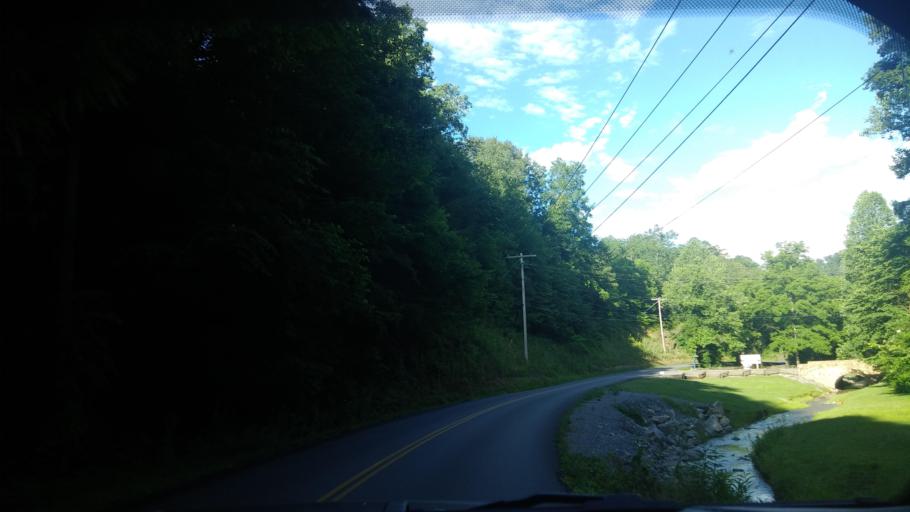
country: US
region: Tennessee
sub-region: Sevier County
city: Pigeon Forge
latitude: 35.7671
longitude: -83.5987
